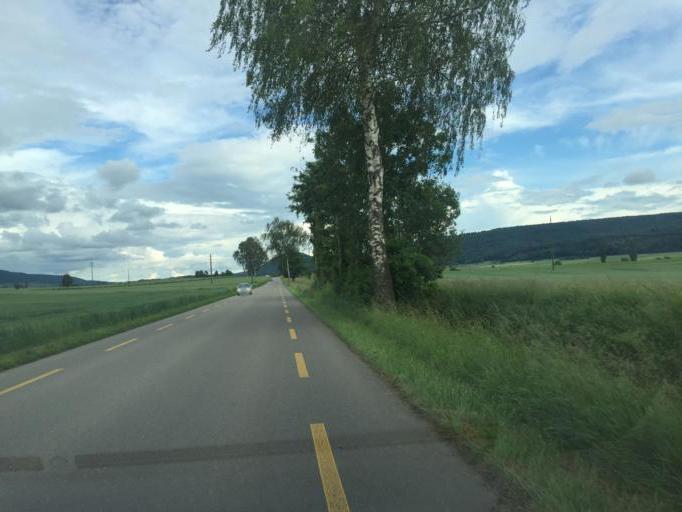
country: CH
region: Schaffhausen
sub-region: Bezirk Unterklettgau
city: Hallau
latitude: 47.6931
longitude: 8.4710
